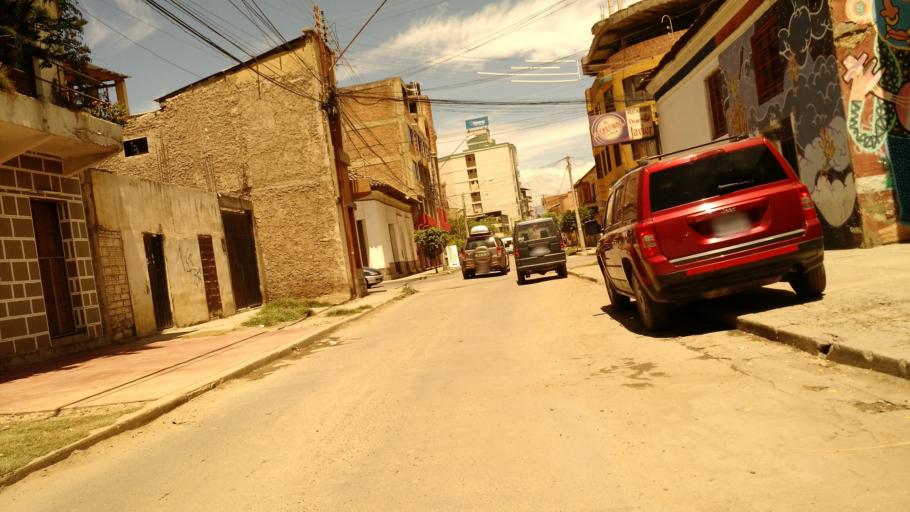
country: BO
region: Cochabamba
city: Cochabamba
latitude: -17.3966
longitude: -66.1641
